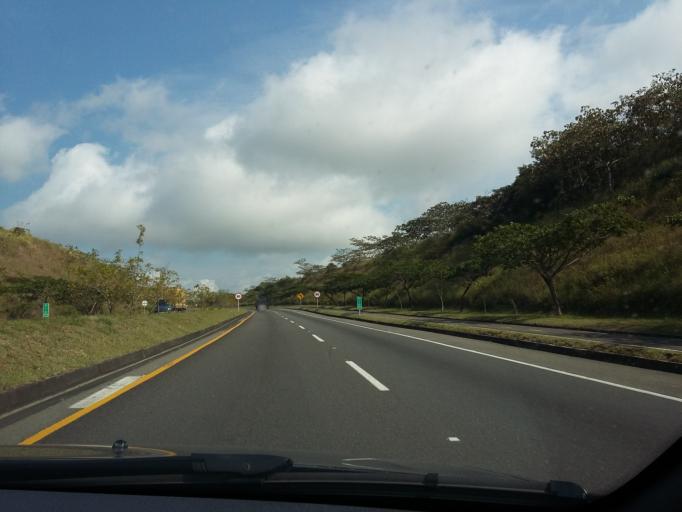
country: CO
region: Tolima
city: Ibague
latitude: 4.3515
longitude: -75.1093
